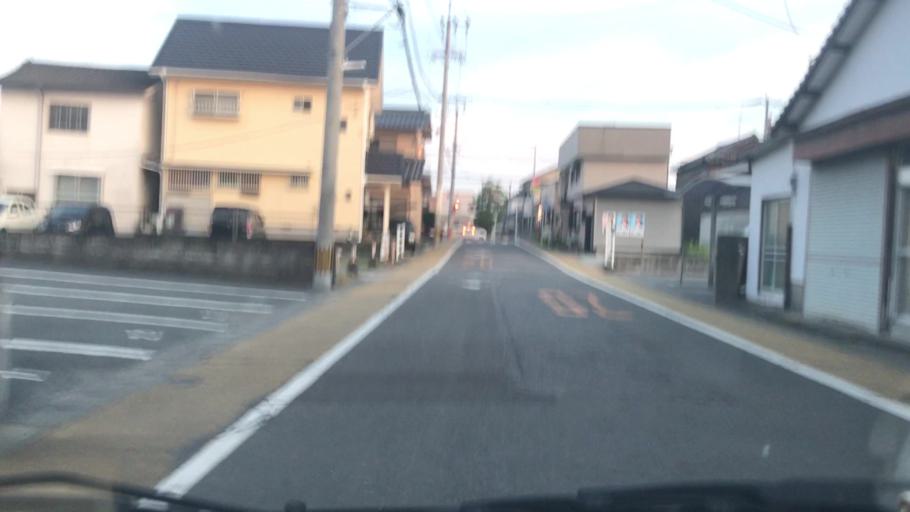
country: JP
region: Saga Prefecture
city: Saga-shi
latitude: 33.2488
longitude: 130.2809
